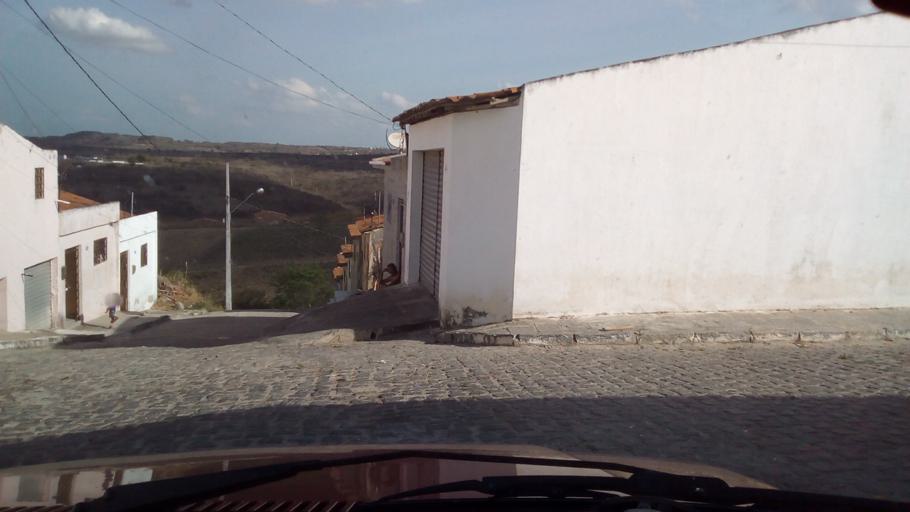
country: BR
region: Paraiba
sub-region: Arara
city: Arara
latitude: -6.8327
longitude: -35.7611
